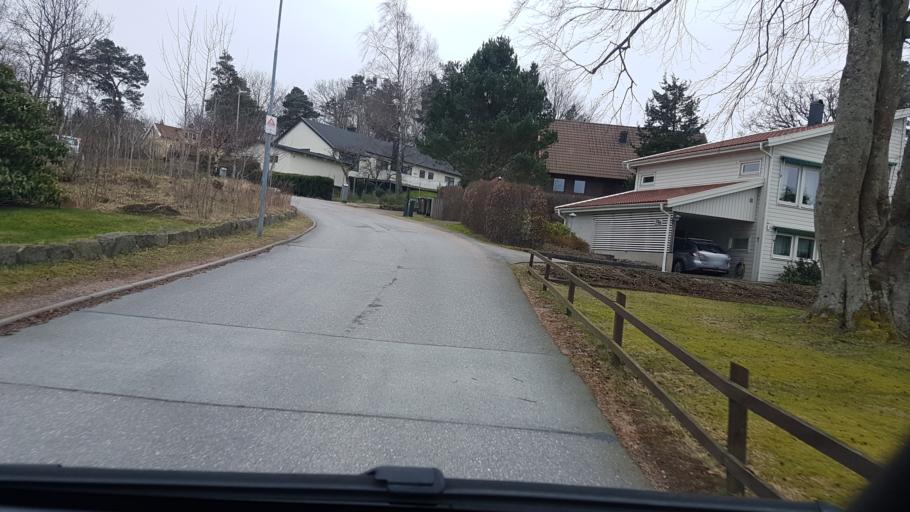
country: SE
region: Vaestra Goetaland
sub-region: Lerums Kommun
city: Lerum
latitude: 57.7685
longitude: 12.2790
